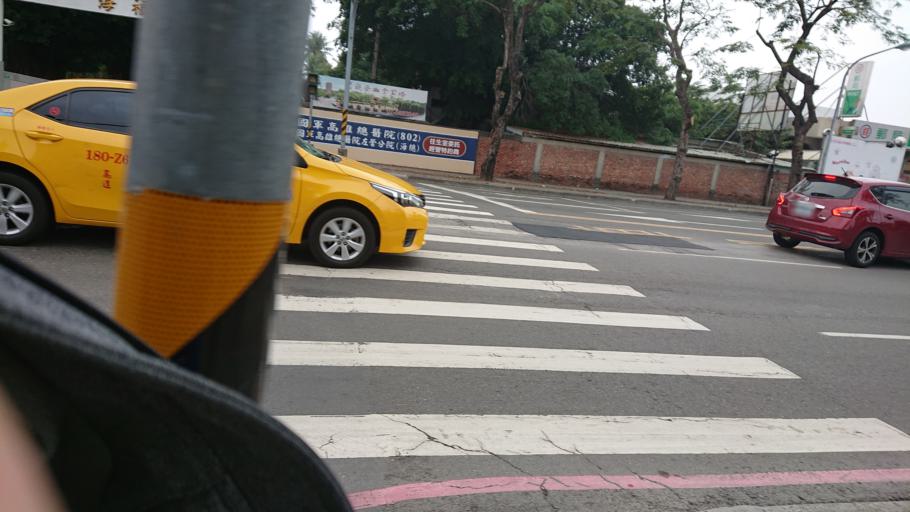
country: TW
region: Kaohsiung
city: Kaohsiung
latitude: 22.7042
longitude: 120.2926
